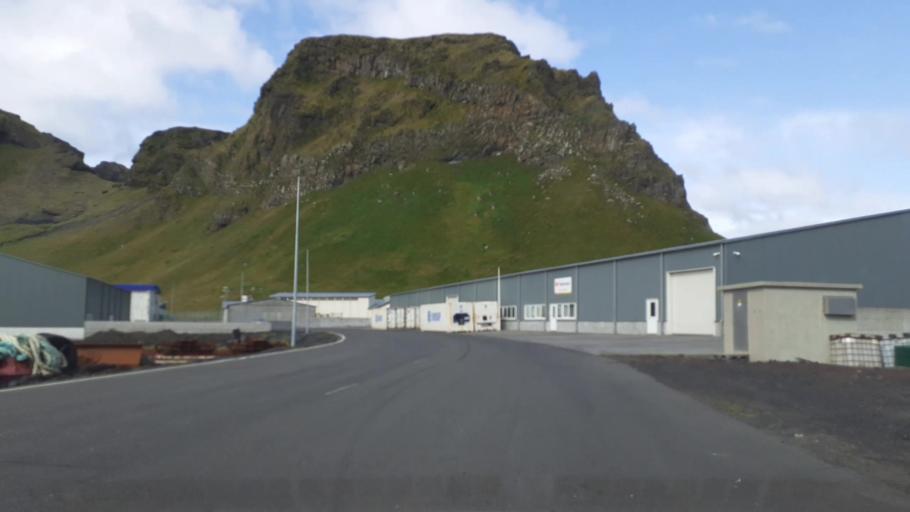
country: IS
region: South
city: Vestmannaeyjar
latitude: 63.4474
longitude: -20.2747
